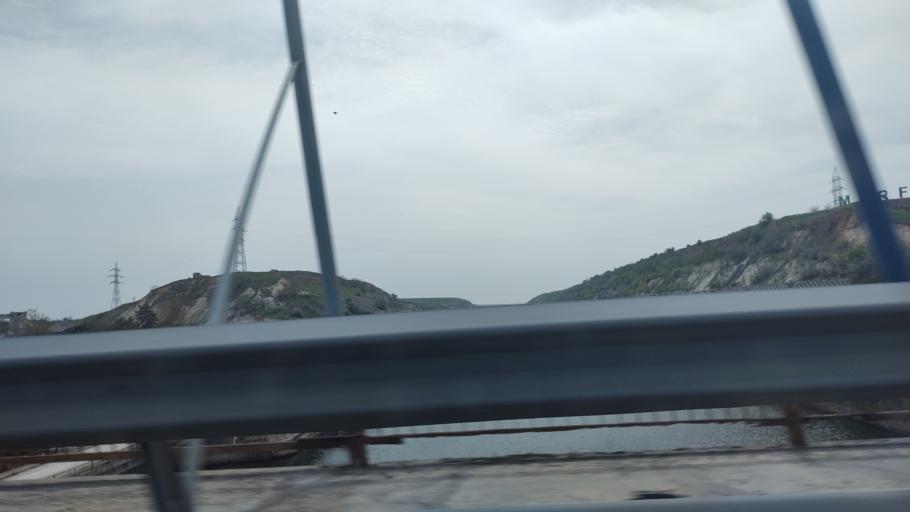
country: RO
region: Constanta
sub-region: Oras Murfatlar
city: Murfatlar
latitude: 44.1699
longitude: 28.4085
